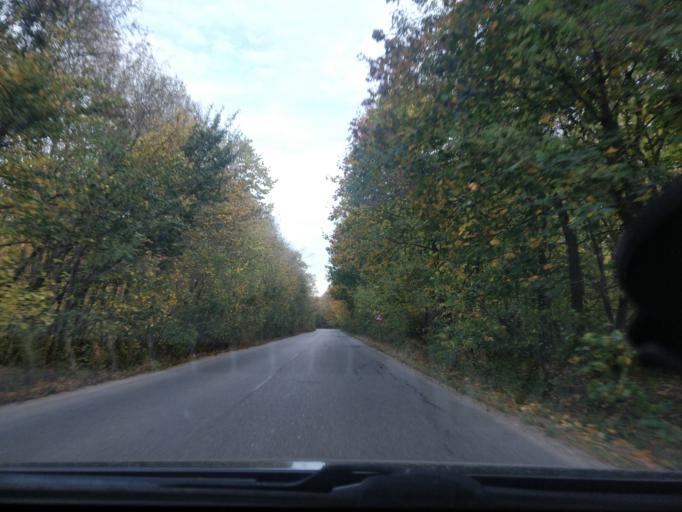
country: RO
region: Giurgiu
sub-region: Comuna Crevedia Mare
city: Dealu
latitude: 44.4301
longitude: 25.6684
